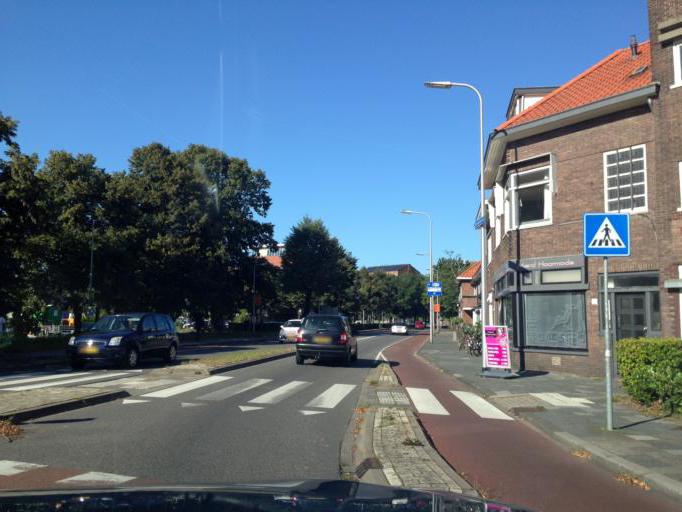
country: NL
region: Overijssel
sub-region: Gemeente Zwolle
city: Zwolle
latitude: 52.5163
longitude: 6.0932
